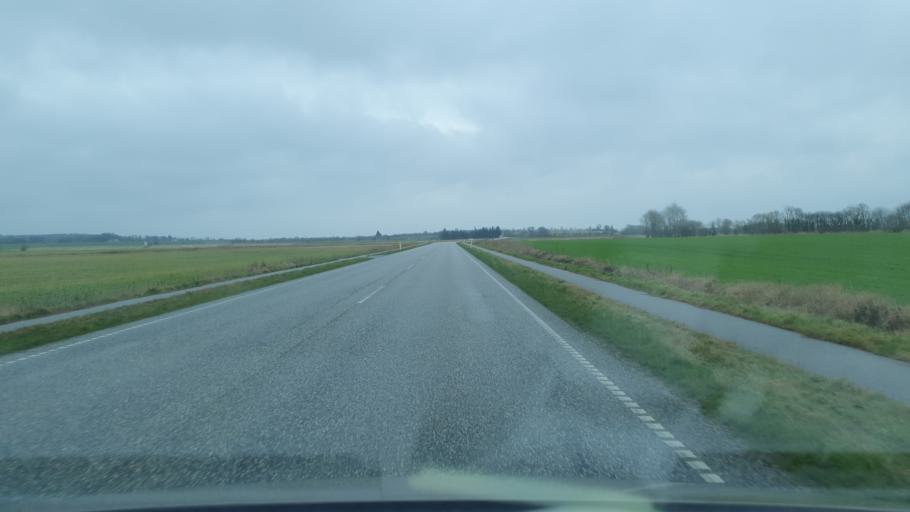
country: DK
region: North Denmark
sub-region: Jammerbugt Kommune
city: Fjerritslev
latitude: 57.1022
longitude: 9.1319
